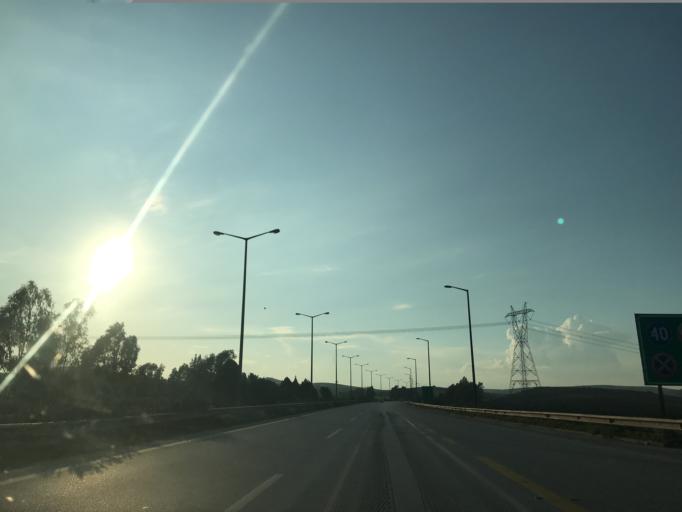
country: TR
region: Osmaniye
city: Toprakkale
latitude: 36.9754
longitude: 36.0142
